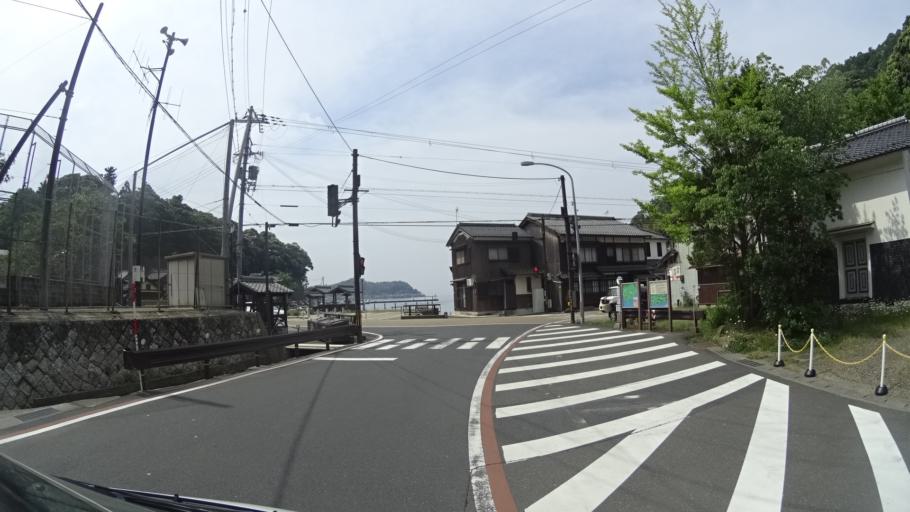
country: JP
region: Kyoto
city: Miyazu
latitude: 35.6761
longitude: 135.2875
